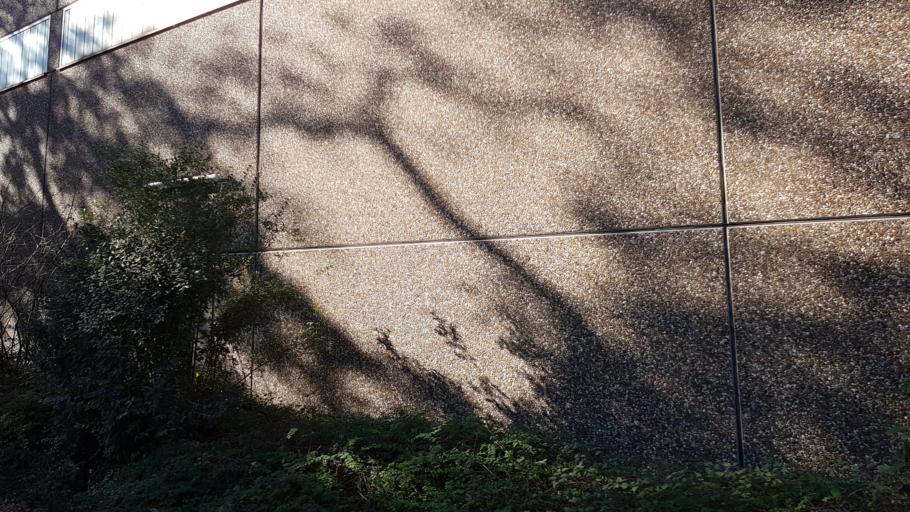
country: DE
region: North Rhine-Westphalia
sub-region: Regierungsbezirk Dusseldorf
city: Muelheim (Ruhr)
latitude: 51.4418
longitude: 6.8647
